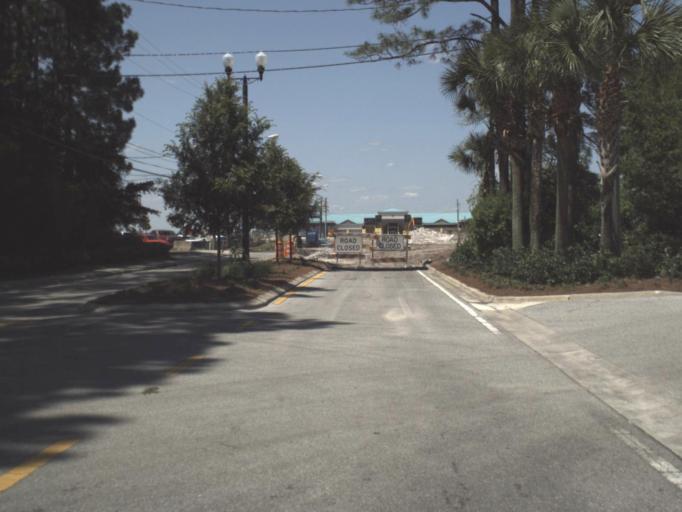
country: US
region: Florida
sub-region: Bay County
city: Pretty Bayou
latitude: 30.2037
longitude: -85.6832
